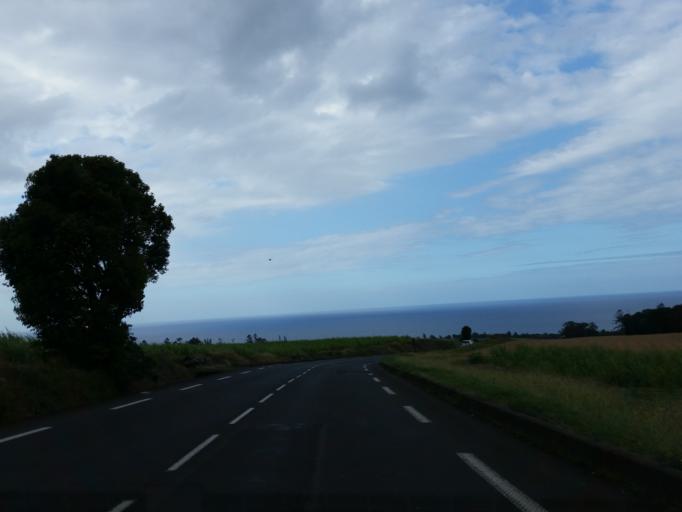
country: RE
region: Reunion
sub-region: Reunion
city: Sainte-Marie
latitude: -20.9154
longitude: 55.5415
